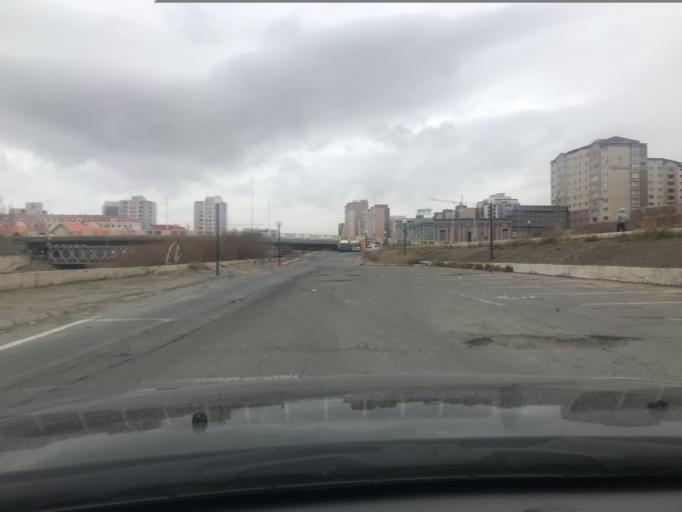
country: MN
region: Ulaanbaatar
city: Ulaanbaatar
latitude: 47.9221
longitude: 106.9321
